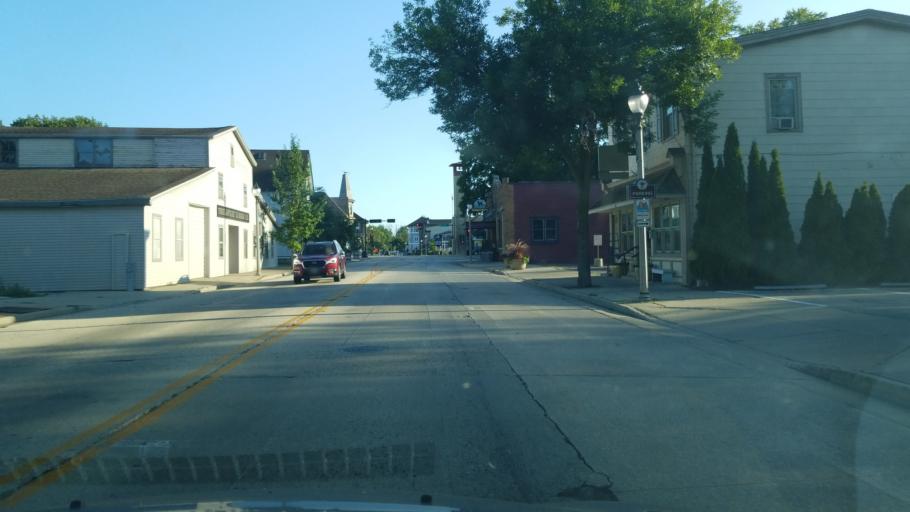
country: US
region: Wisconsin
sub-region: Ozaukee County
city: Mequon
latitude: 43.2292
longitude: -87.9841
